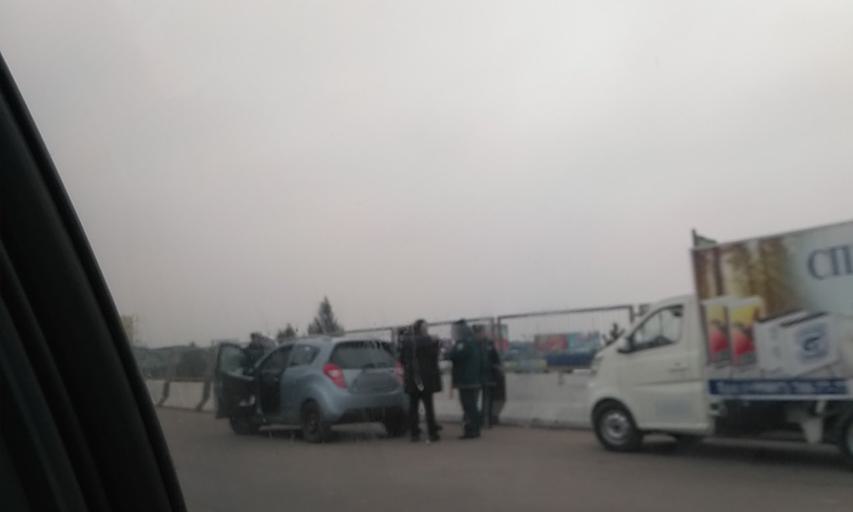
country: UZ
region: Toshkent Shahri
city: Tashkent
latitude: 41.2843
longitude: 69.1489
